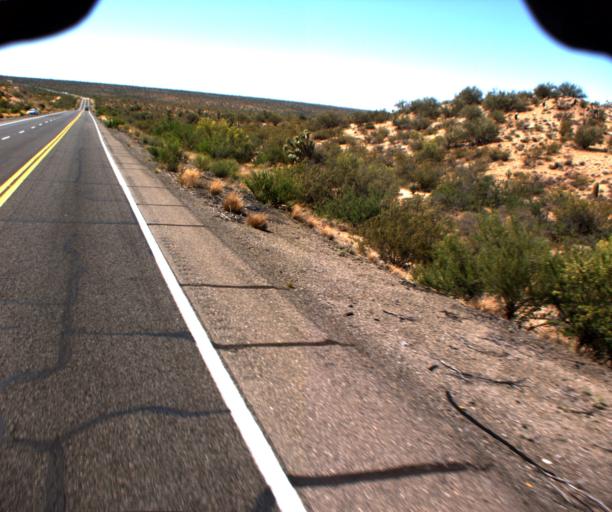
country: US
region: Arizona
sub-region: Yavapai County
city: Congress
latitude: 34.2172
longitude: -113.0677
